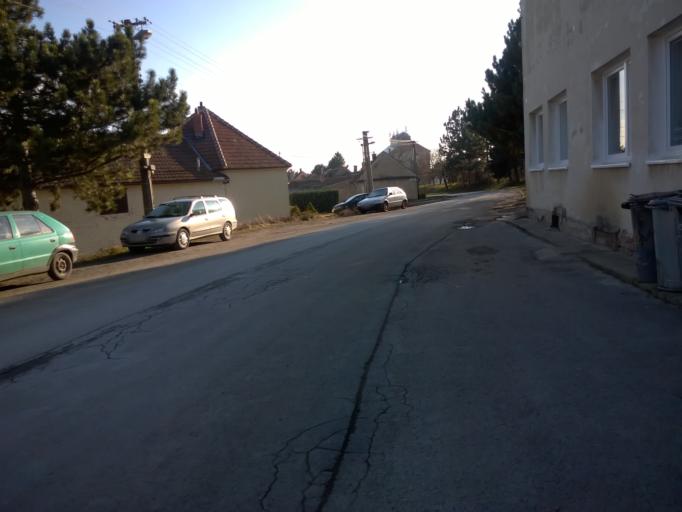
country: CZ
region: South Moravian
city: Krenovice
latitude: 49.1433
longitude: 16.8252
